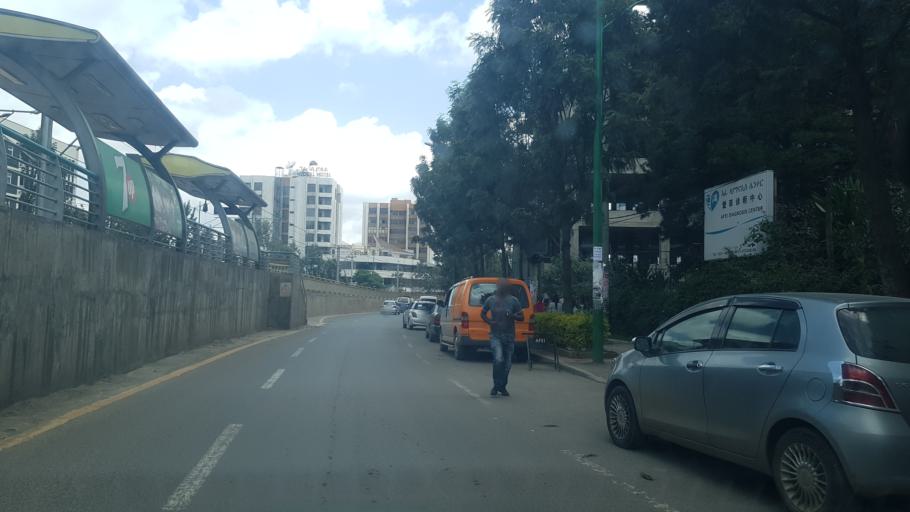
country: ET
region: Adis Abeba
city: Addis Ababa
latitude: 8.9953
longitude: 38.7597
